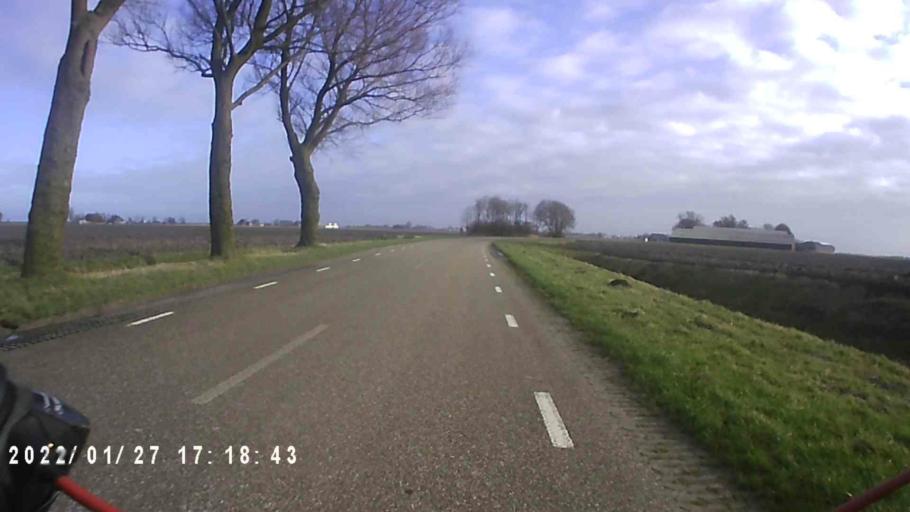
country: NL
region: Friesland
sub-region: Gemeente Dongeradeel
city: Anjum
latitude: 53.3889
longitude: 6.1073
